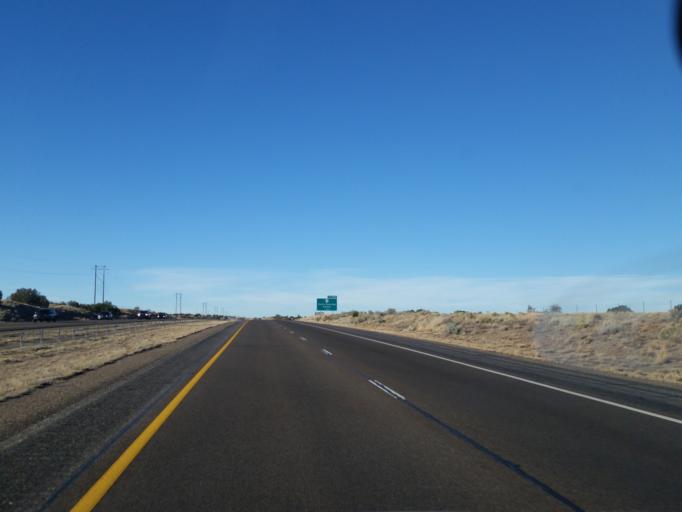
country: US
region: New Mexico
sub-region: Sandoval County
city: Santo Domingo Pueblo
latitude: 35.4798
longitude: -106.2815
